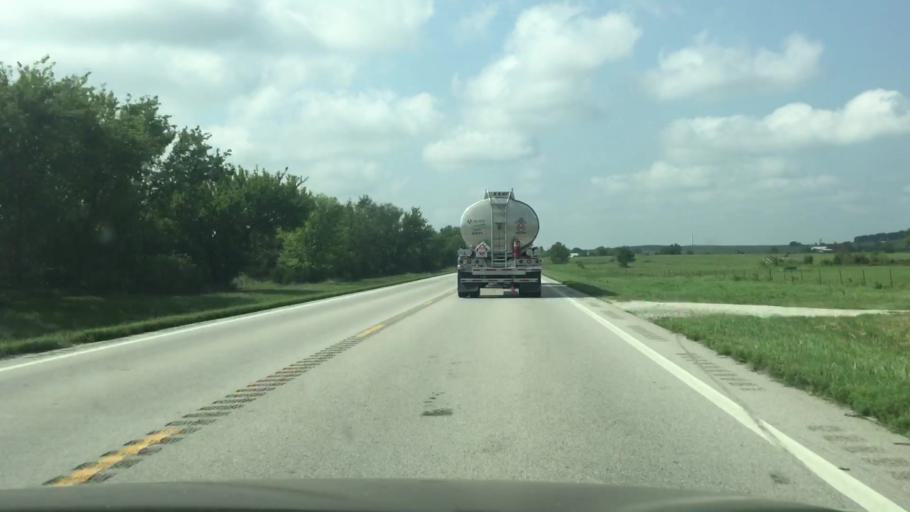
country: US
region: Kansas
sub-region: Allen County
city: Iola
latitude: 38.1036
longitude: -95.3545
